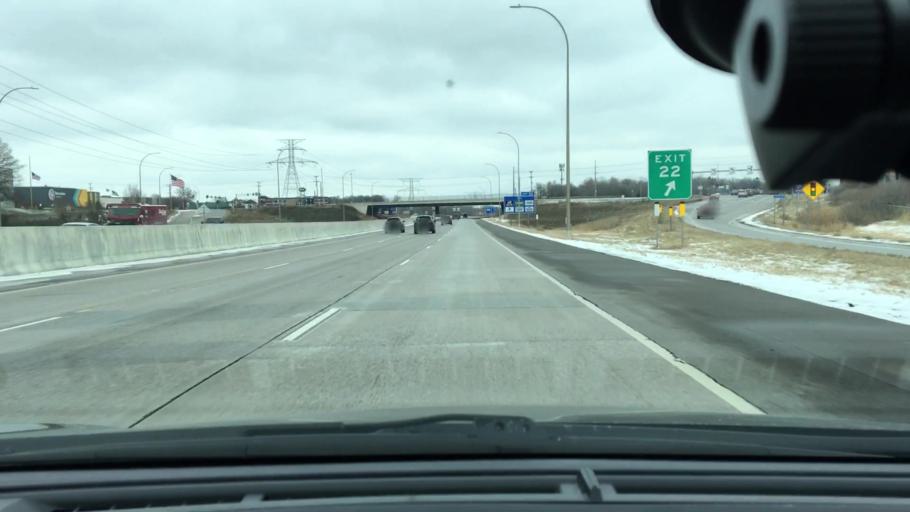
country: US
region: Minnesota
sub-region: Hennepin County
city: Plymouth
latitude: 45.0076
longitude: -93.4571
